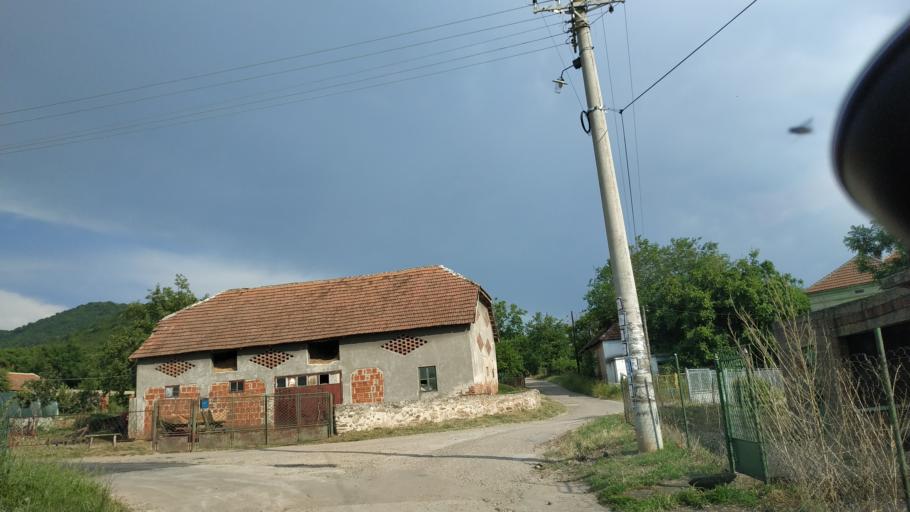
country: RS
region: Central Serbia
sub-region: Nisavski Okrug
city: Aleksinac
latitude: 43.6045
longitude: 21.6936
